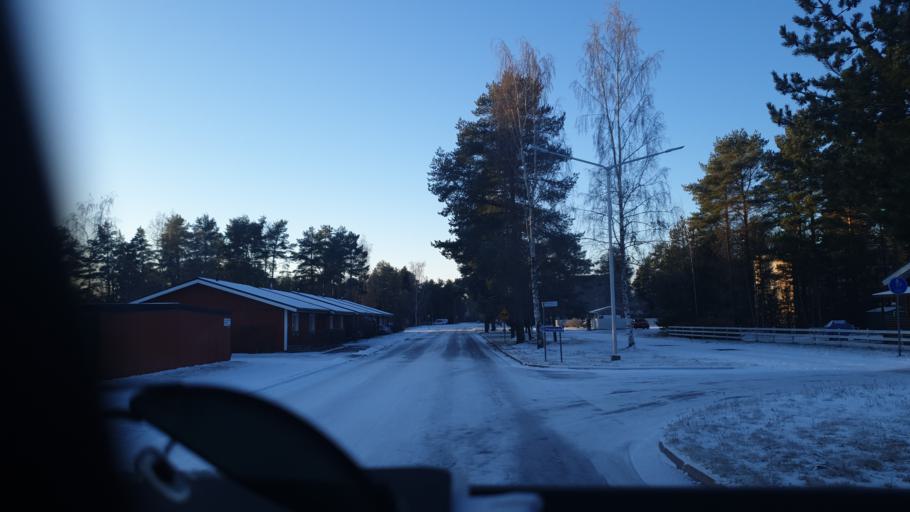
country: FI
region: Central Ostrobothnia
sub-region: Kokkola
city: Kokkola
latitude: 63.8237
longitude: 23.0785
